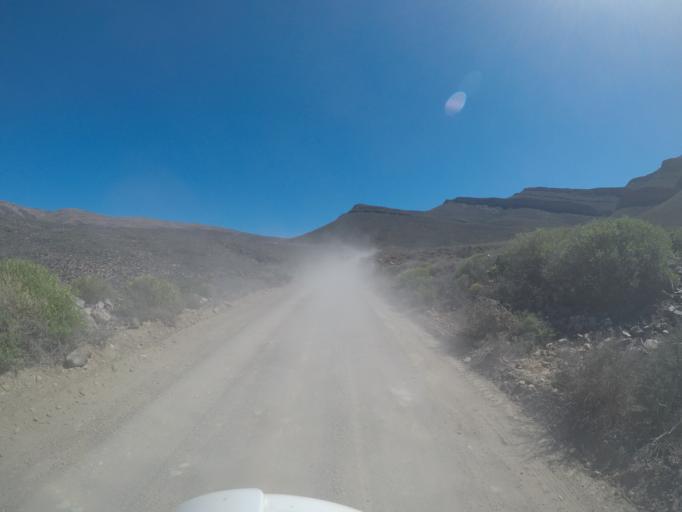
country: ZA
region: Western Cape
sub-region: West Coast District Municipality
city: Clanwilliam
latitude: -32.6227
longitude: 19.3867
